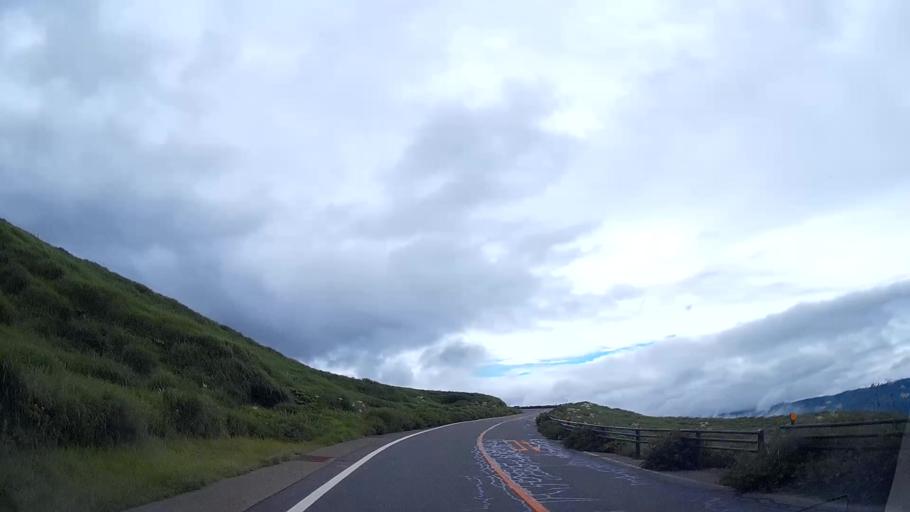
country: JP
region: Kumamoto
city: Aso
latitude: 32.9067
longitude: 131.0581
